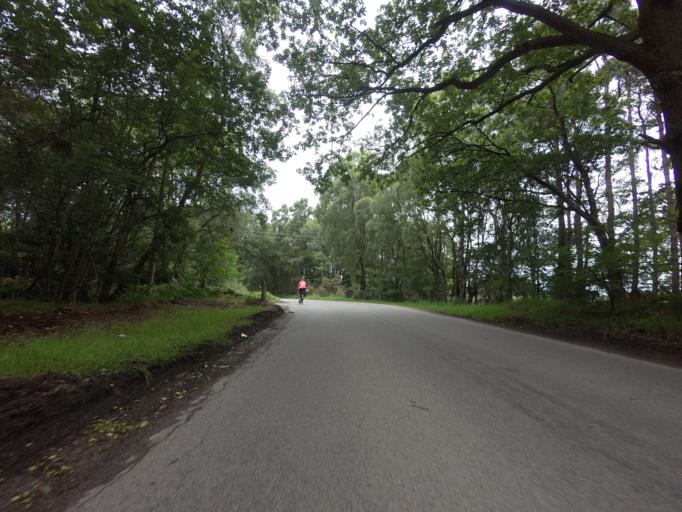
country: GB
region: Scotland
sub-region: Moray
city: Elgin
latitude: 57.6548
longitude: -3.3469
